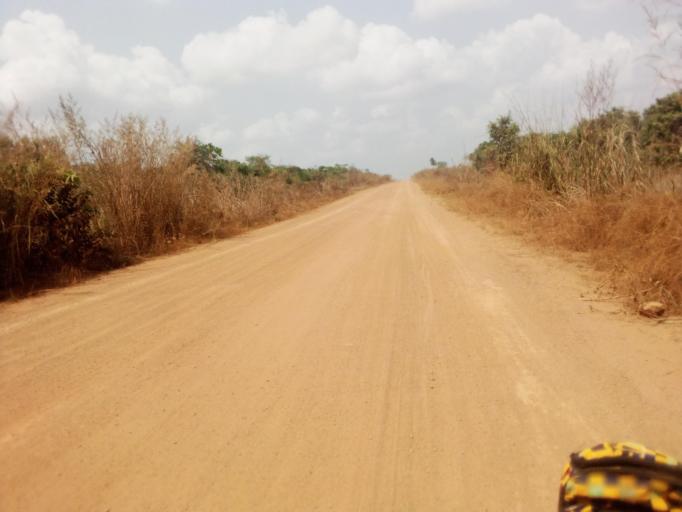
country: SL
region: Southern Province
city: Mogbwemo
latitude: 7.6604
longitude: -12.2665
